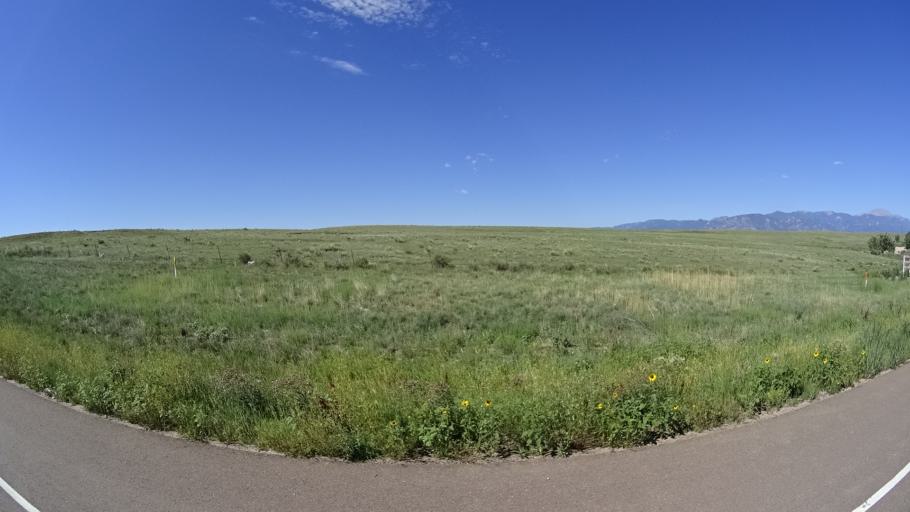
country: US
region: Colorado
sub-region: El Paso County
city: Security-Widefield
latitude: 38.7494
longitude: -104.6513
